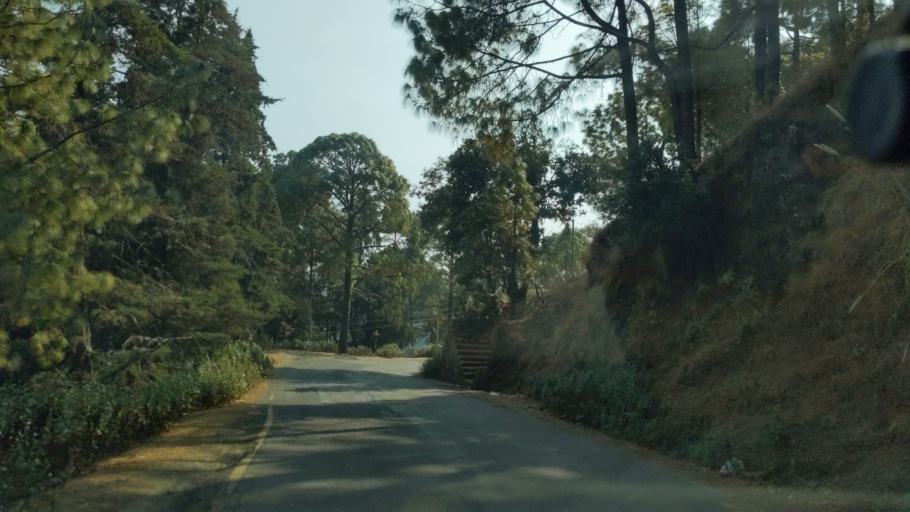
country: IN
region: Uttarakhand
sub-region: Naini Tal
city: Bhowali
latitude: 29.3896
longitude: 79.5401
